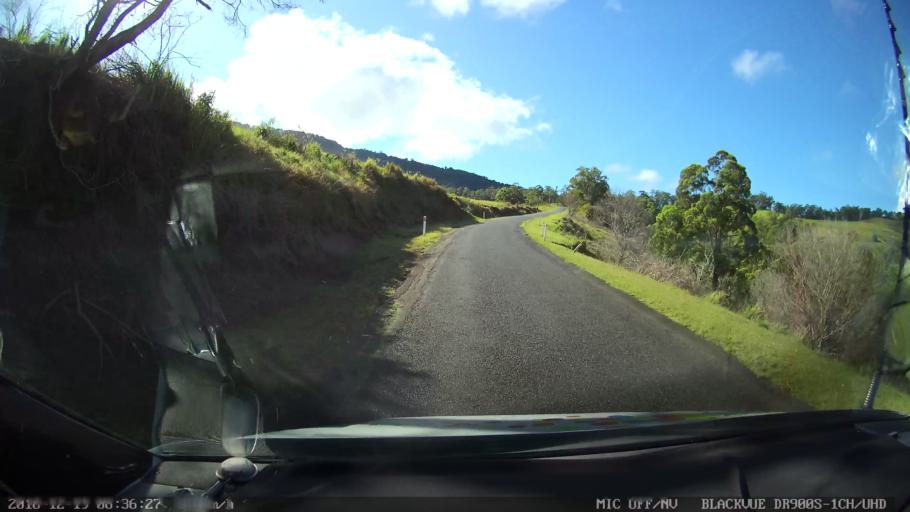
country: AU
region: New South Wales
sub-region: Kyogle
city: Kyogle
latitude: -28.3258
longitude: 152.9730
